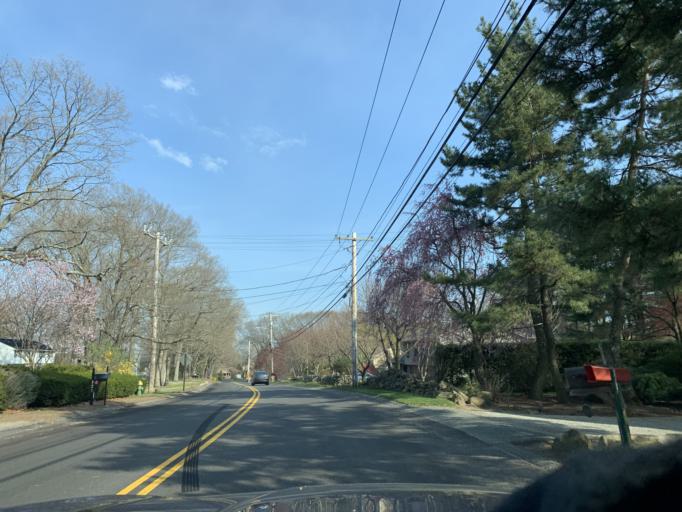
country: US
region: Rhode Island
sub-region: Providence County
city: Johnston
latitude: 41.7671
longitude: -71.5021
